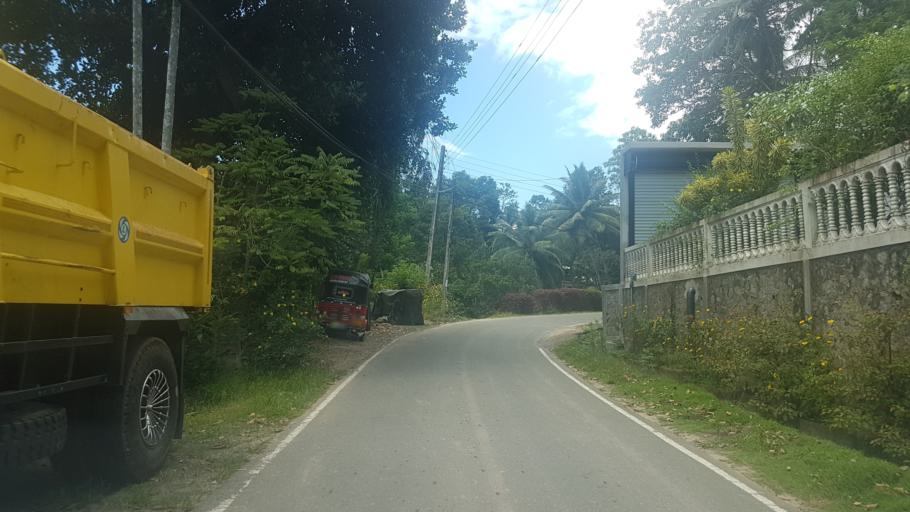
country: LK
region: Central
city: Gampola
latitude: 7.2150
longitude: 80.5916
